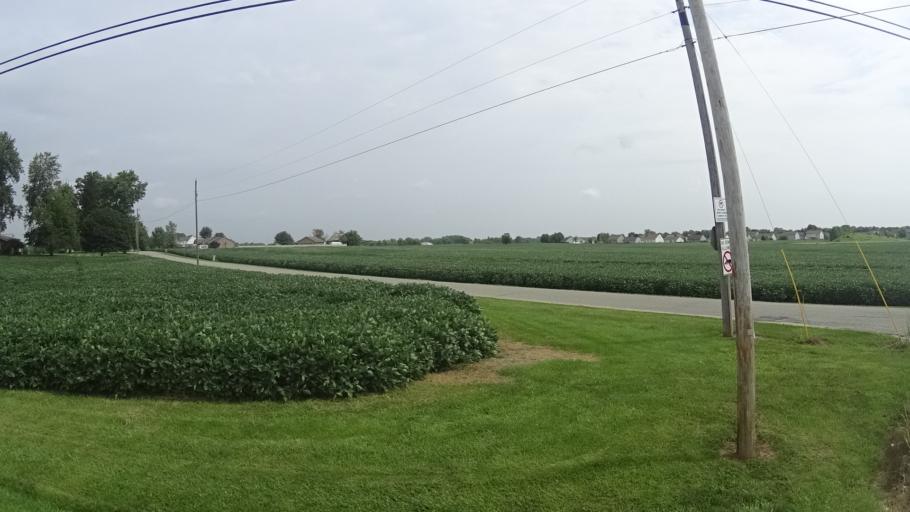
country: US
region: Indiana
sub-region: Madison County
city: Pendleton
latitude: 40.0105
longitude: -85.7537
